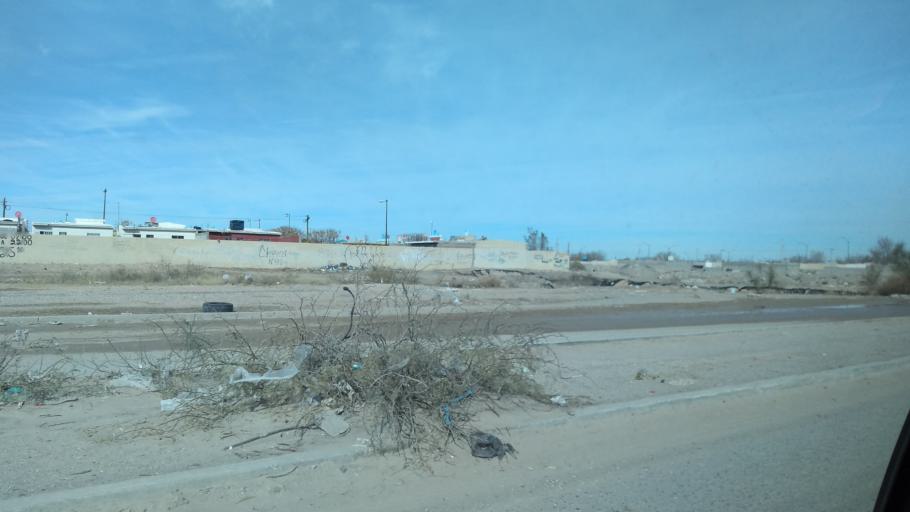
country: US
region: Texas
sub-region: El Paso County
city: San Elizario
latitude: 31.5747
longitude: -106.3459
